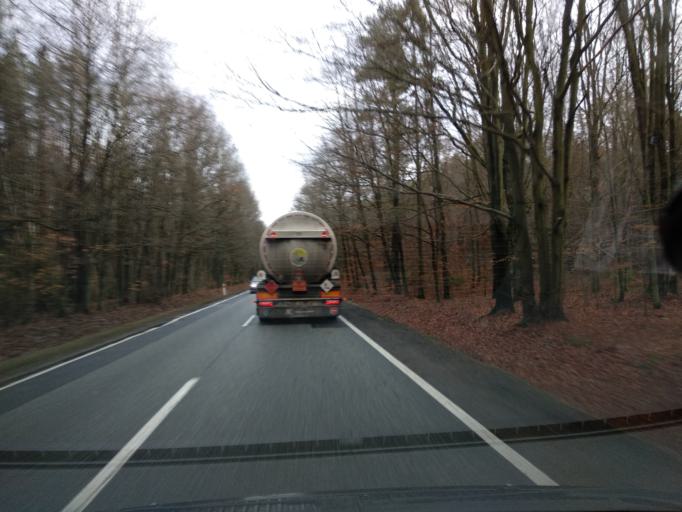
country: PL
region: Lower Silesian Voivodeship
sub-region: Powiat olesnicki
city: Twardogora
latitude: 51.3170
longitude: 17.5581
